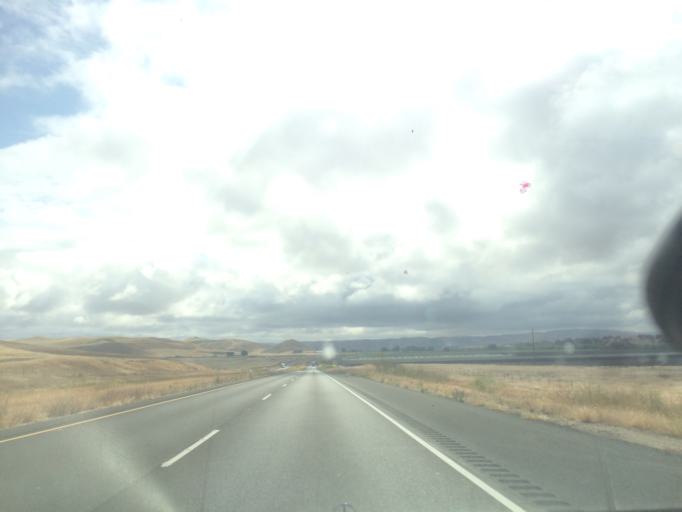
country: US
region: California
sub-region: San Luis Obispo County
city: Shandon
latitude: 35.6609
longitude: -120.4443
